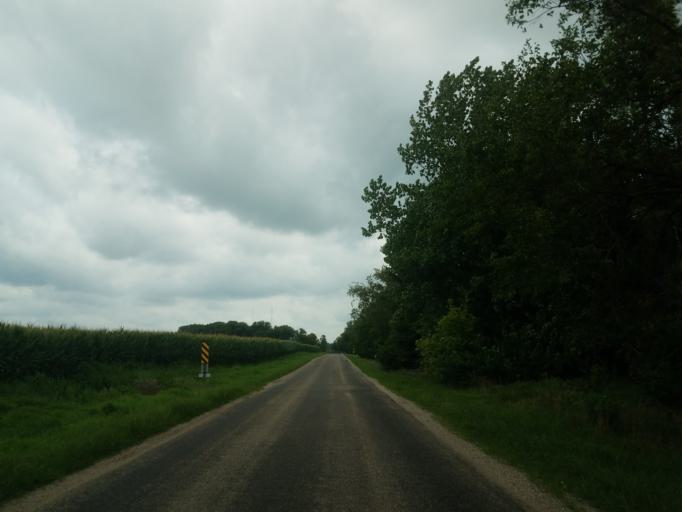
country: US
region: Illinois
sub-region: McLean County
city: Twin Grove
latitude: 40.4626
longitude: -89.0423
